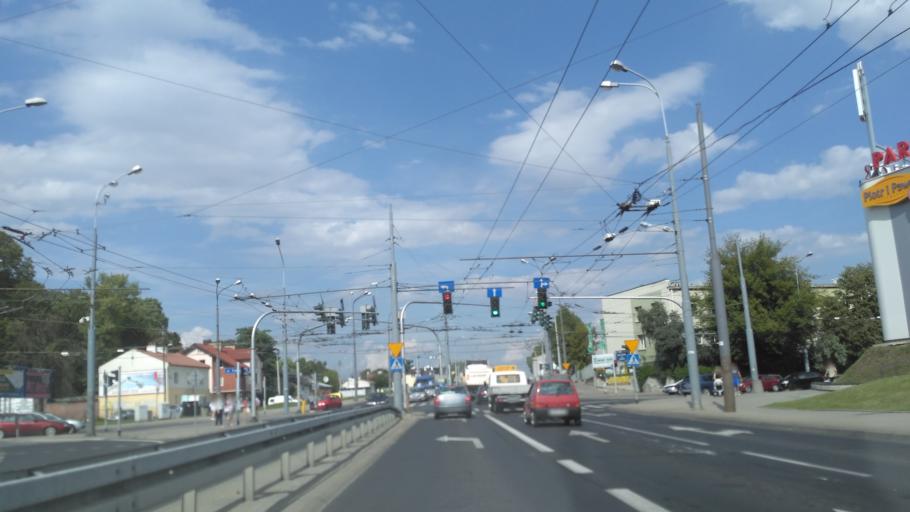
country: PL
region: Lublin Voivodeship
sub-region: Powiat lubelski
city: Lublin
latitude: 51.2361
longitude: 22.5761
